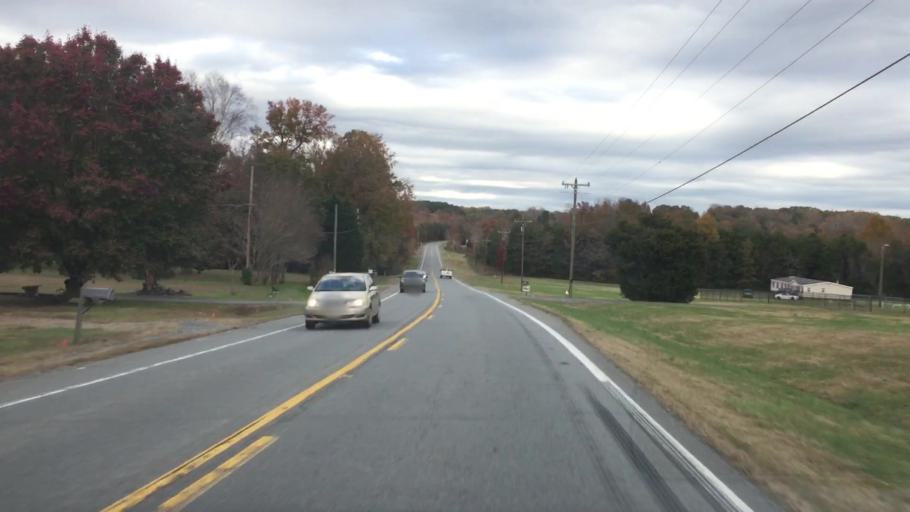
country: US
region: North Carolina
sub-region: Rockingham County
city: Reidsville
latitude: 36.3010
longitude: -79.7233
